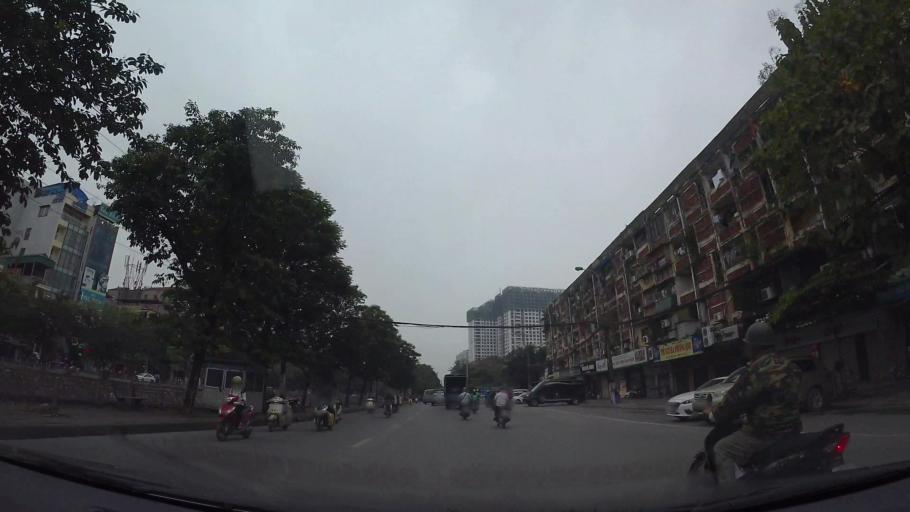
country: VN
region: Ha Noi
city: Hai BaTrung
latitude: 21.0019
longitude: 105.8614
